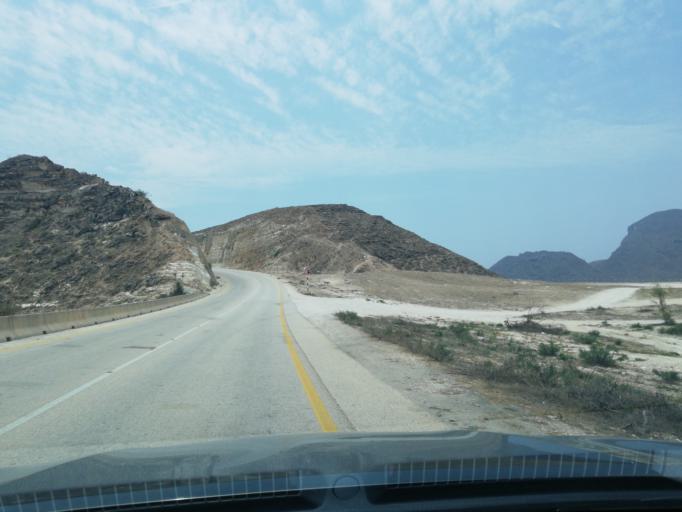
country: OM
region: Zufar
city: Salalah
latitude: 16.8809
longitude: 53.7462
